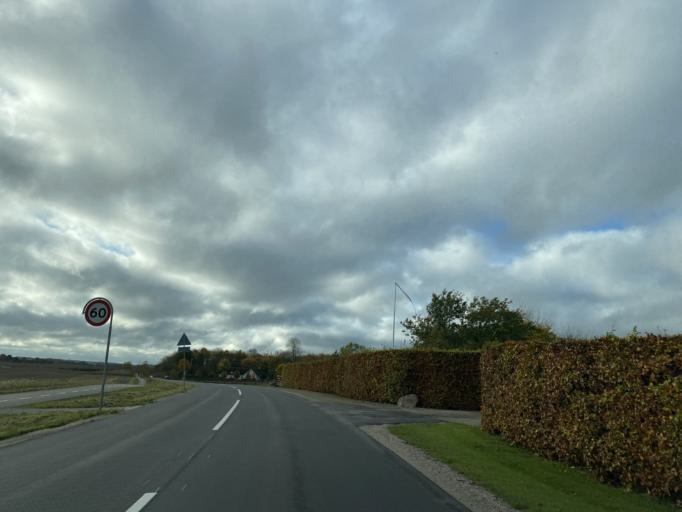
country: DK
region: Central Jutland
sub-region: Favrskov Kommune
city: Hammel
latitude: 56.2550
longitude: 9.8366
